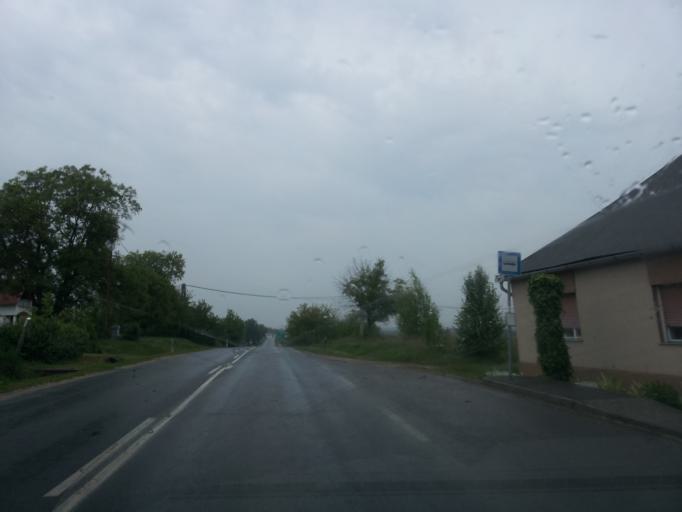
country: HU
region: Tolna
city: Szekszard
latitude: 46.3030
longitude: 18.6906
